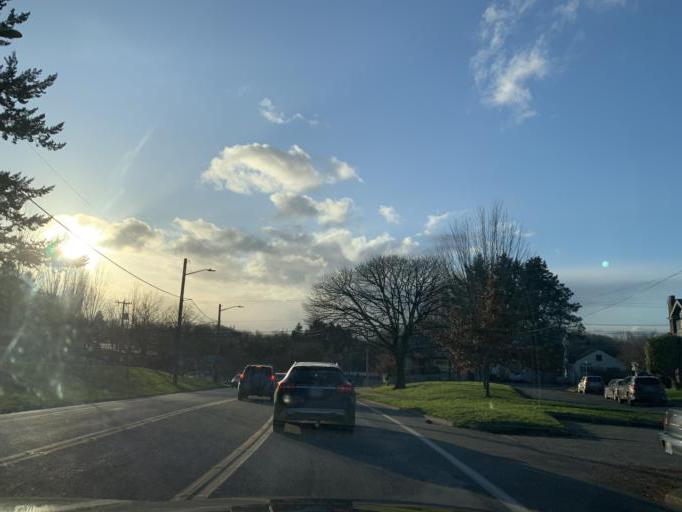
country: US
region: Washington
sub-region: King County
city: Seattle
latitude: 47.5720
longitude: -122.3115
